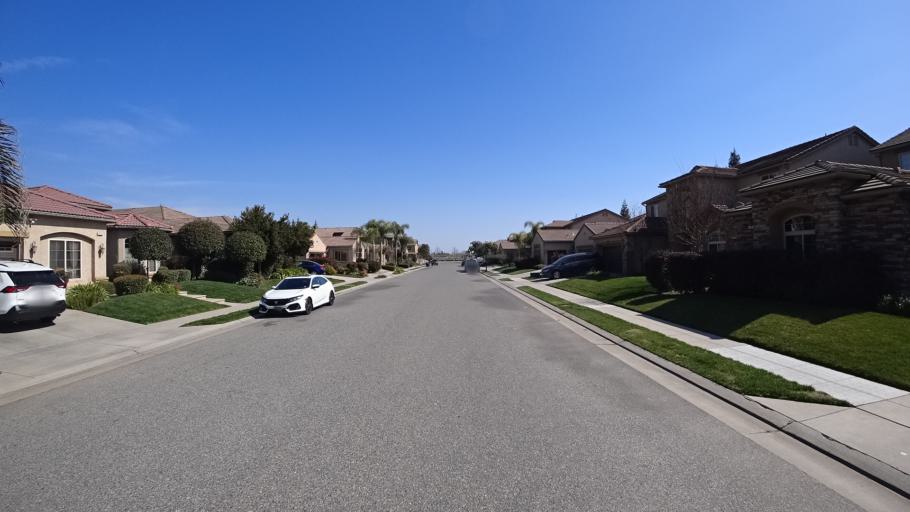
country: US
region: California
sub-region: Fresno County
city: Clovis
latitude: 36.8972
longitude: -119.7588
